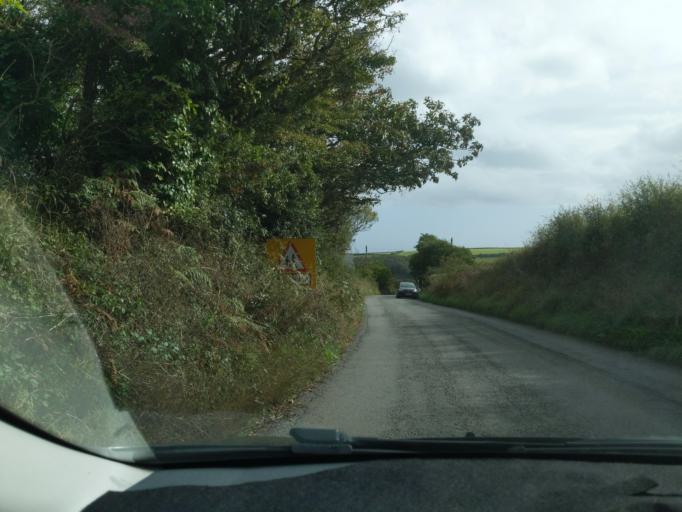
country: GB
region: England
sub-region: Cornwall
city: Mevagissey
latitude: 50.2449
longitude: -4.8010
